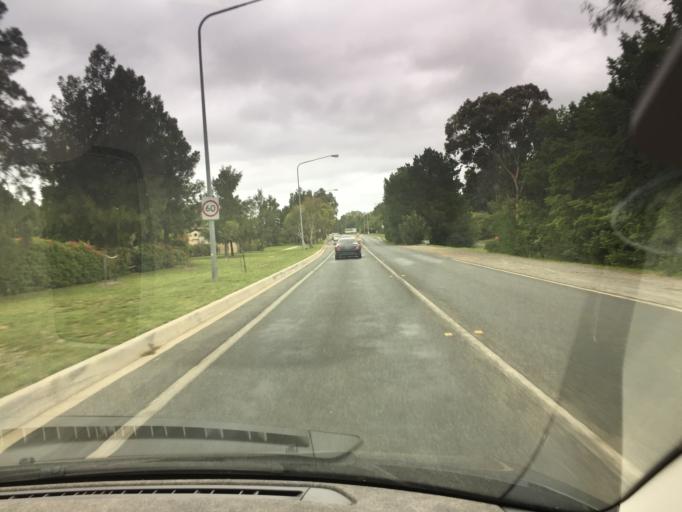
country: AU
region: Australian Capital Territory
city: Kaleen
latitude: -35.2340
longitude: 149.1253
